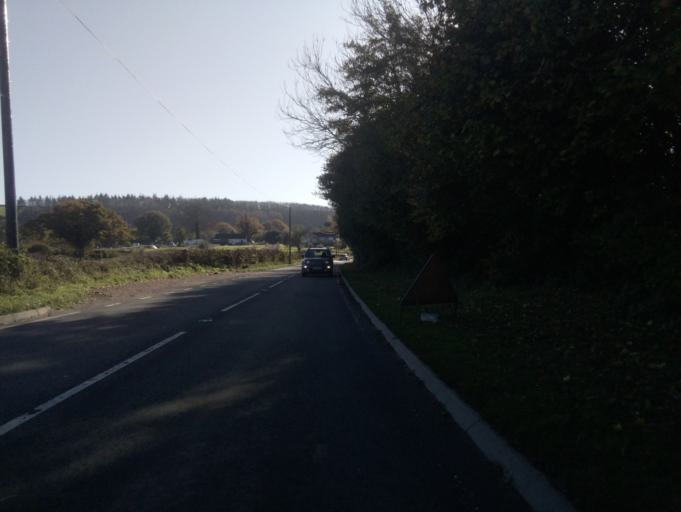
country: GB
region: England
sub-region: Dorset
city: Sherborne
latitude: 50.8502
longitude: -2.4622
